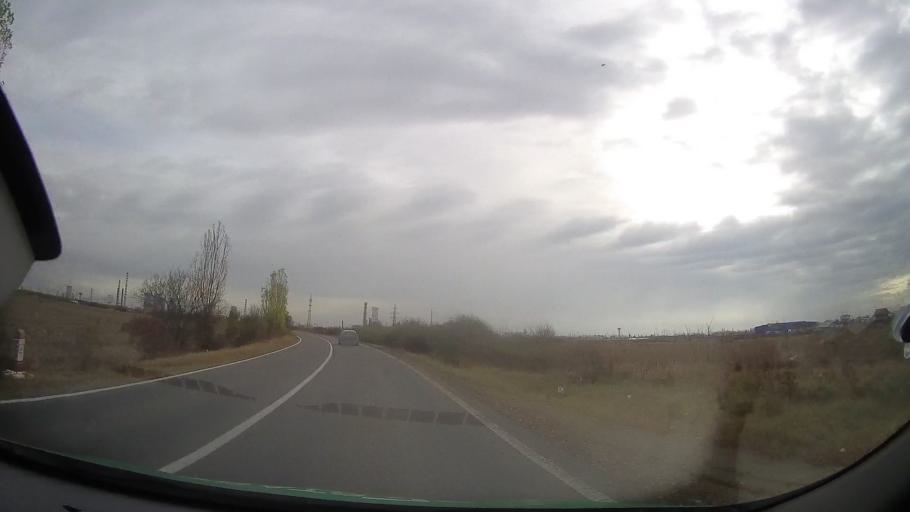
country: RO
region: Prahova
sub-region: Comuna Bucov
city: Bucov
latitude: 44.9536
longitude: 26.0537
